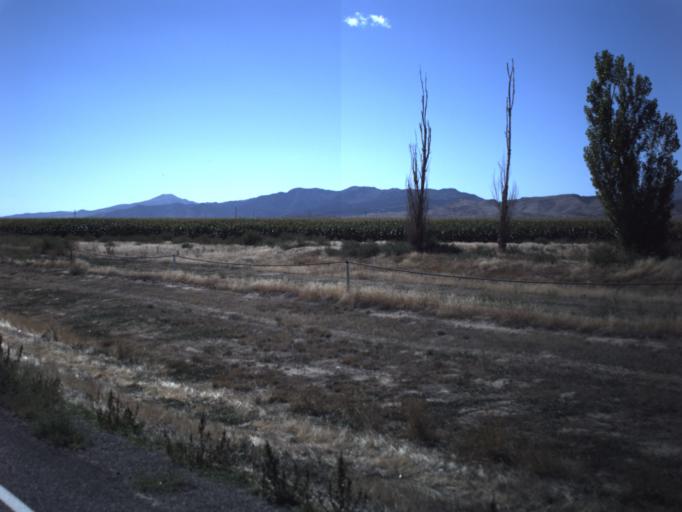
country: US
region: Utah
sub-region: Utah County
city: Genola
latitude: 40.0071
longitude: -111.9581
